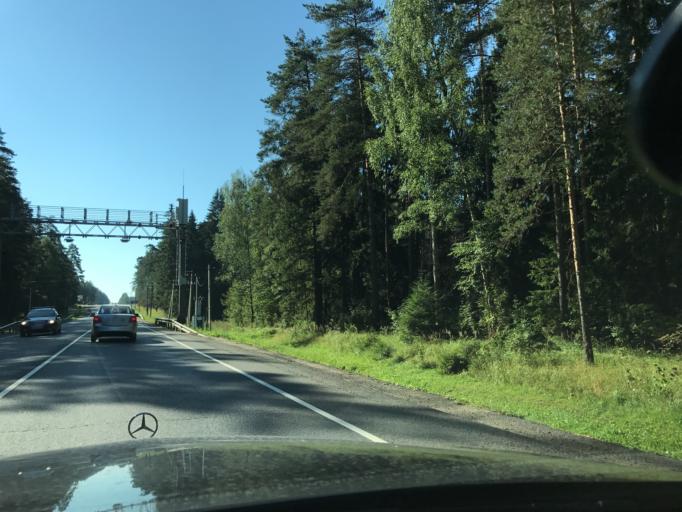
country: RU
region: Moskovskaya
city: Noginsk-9
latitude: 56.0973
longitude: 38.6703
